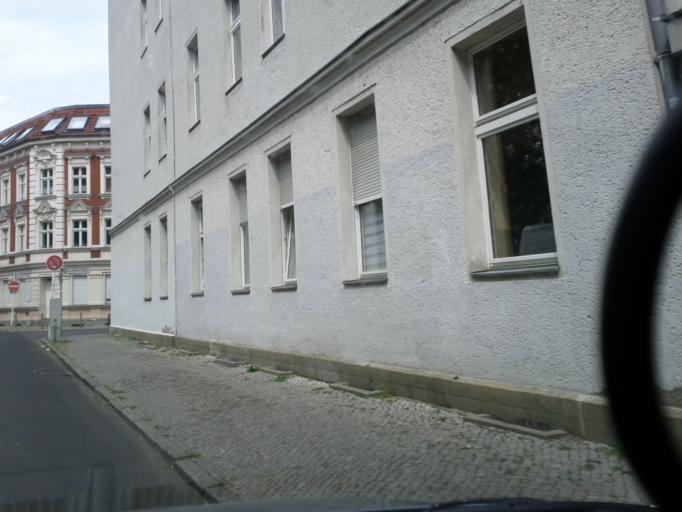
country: DE
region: Berlin
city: Kopenick Bezirk
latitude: 52.4429
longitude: 13.5670
